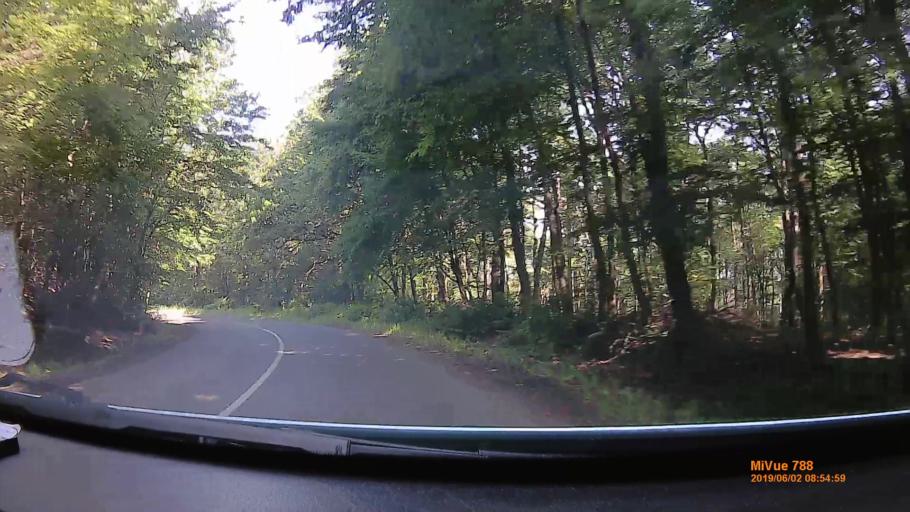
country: HU
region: Borsod-Abauj-Zemplen
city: Sajobabony
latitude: 48.1537
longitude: 20.6670
